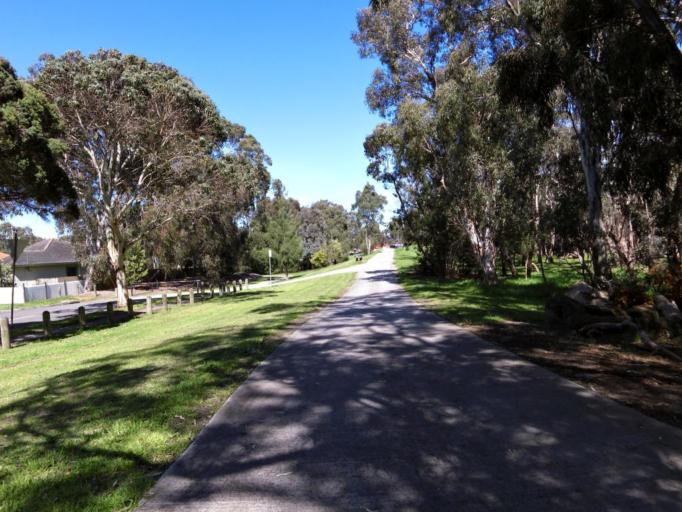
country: AU
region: Victoria
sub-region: Greater Dandenong
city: Dandenong
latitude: -37.9762
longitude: 145.1953
